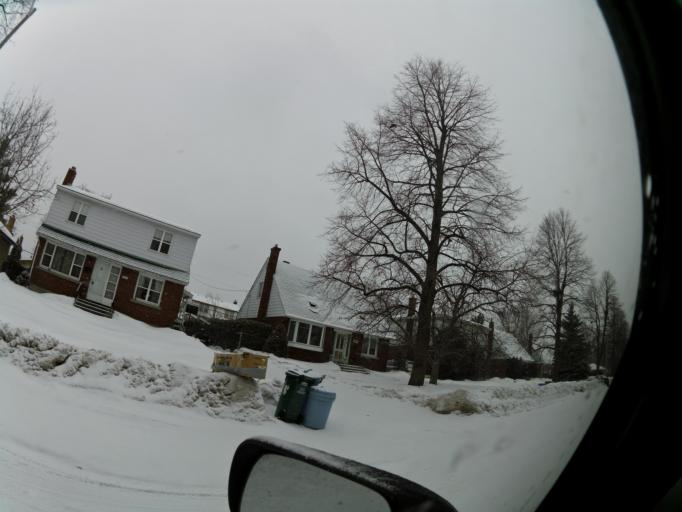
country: CA
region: Ontario
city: Ottawa
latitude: 45.4060
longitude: -75.6393
